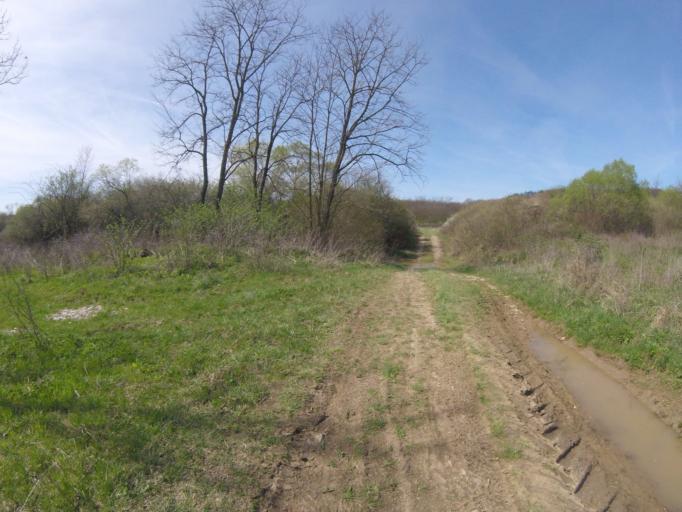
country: HU
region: Borsod-Abauj-Zemplen
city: Szendro
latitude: 48.4195
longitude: 20.7577
